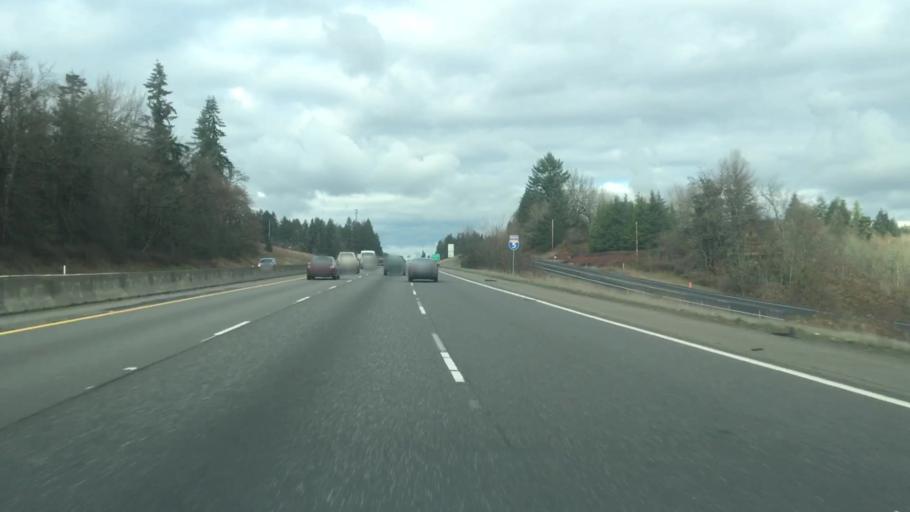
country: US
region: Washington
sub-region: Lewis County
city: Winlock
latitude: 46.4218
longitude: -122.8910
